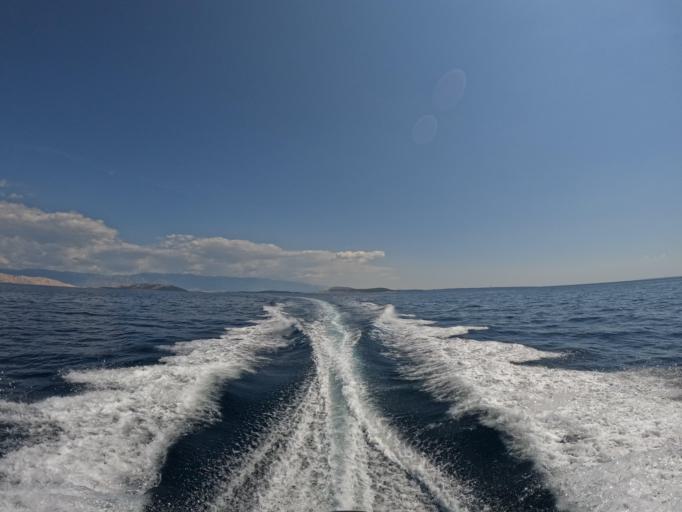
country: HR
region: Primorsko-Goranska
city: Lopar
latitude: 44.8856
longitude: 14.6415
